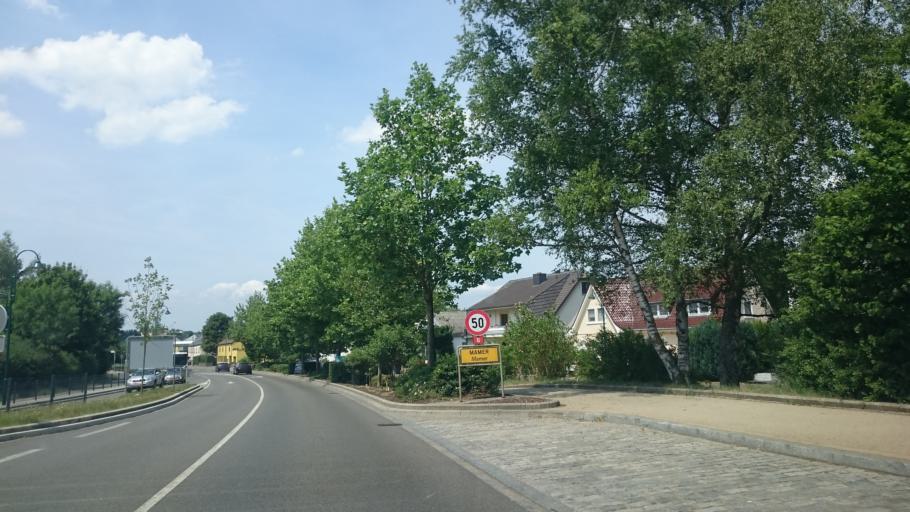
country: LU
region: Luxembourg
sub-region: Canton de Capellen
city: Mamer
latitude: 49.6246
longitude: 6.0365
